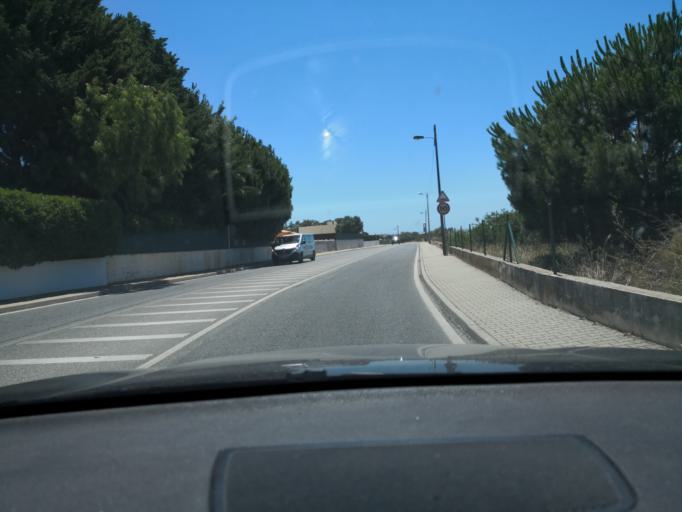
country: PT
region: Faro
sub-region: Albufeira
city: Ferreiras
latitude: 37.1073
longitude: -8.2004
